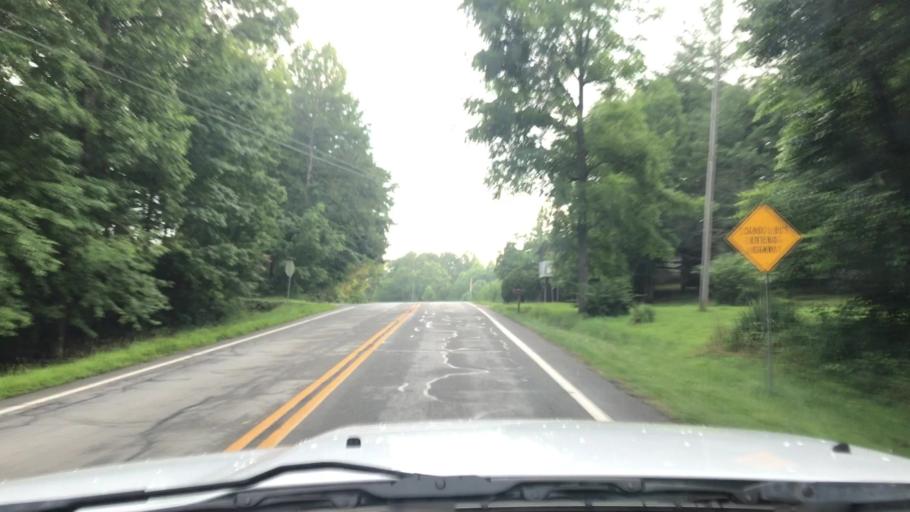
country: US
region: Georgia
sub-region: Fannin County
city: Blue Ridge
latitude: 34.9804
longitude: -84.1946
